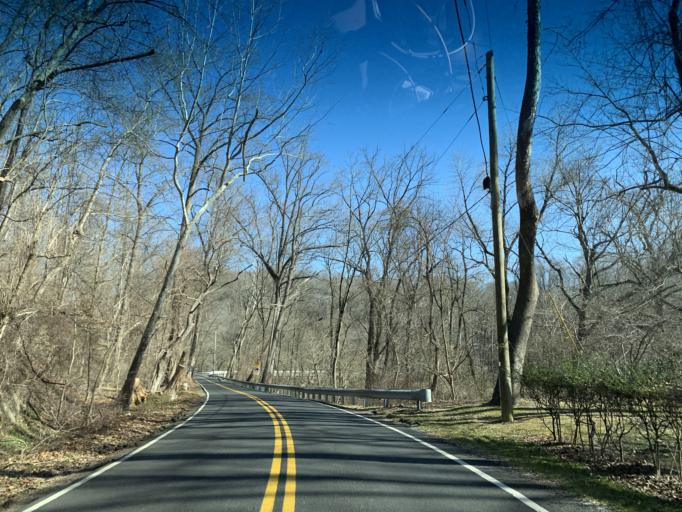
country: US
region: Maryland
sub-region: Cecil County
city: Rising Sun
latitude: 39.6609
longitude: -76.1495
